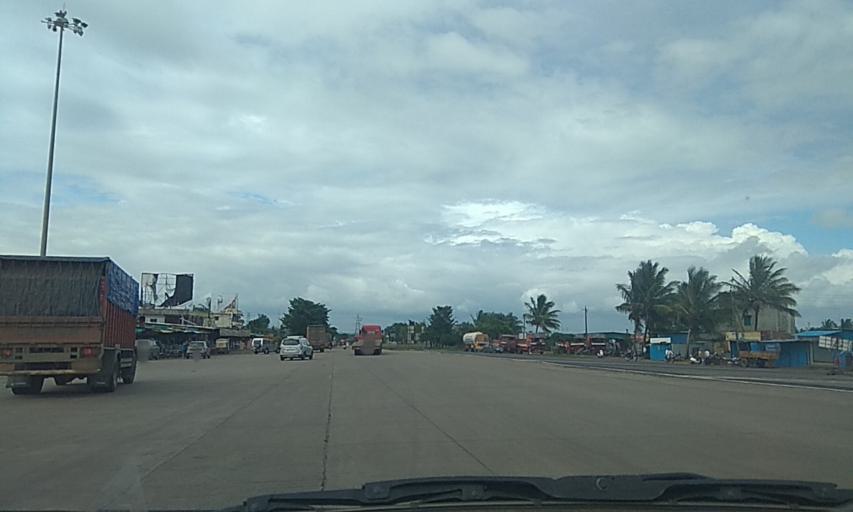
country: IN
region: Maharashtra
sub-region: Kolhapur
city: Kagal
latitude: 16.5432
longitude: 74.3181
